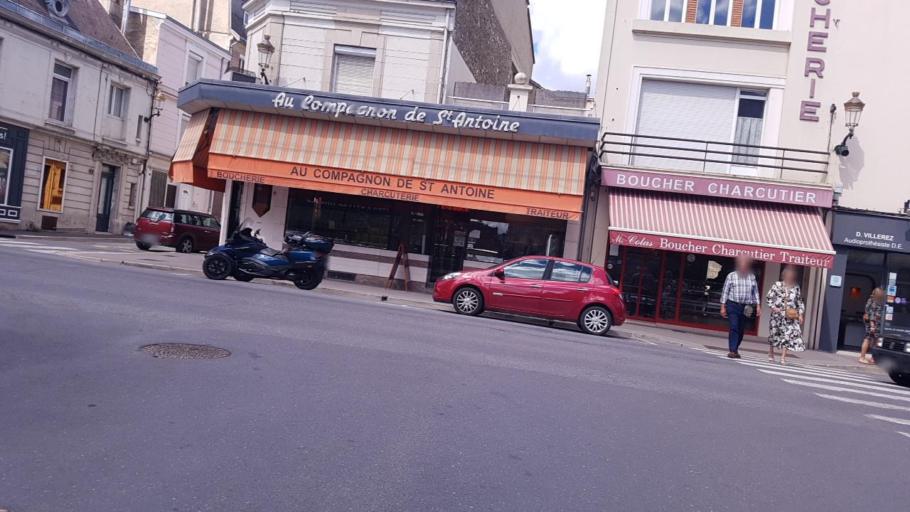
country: FR
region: Champagne-Ardenne
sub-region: Departement de la Marne
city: Epernay
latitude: 49.0454
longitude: 3.9551
